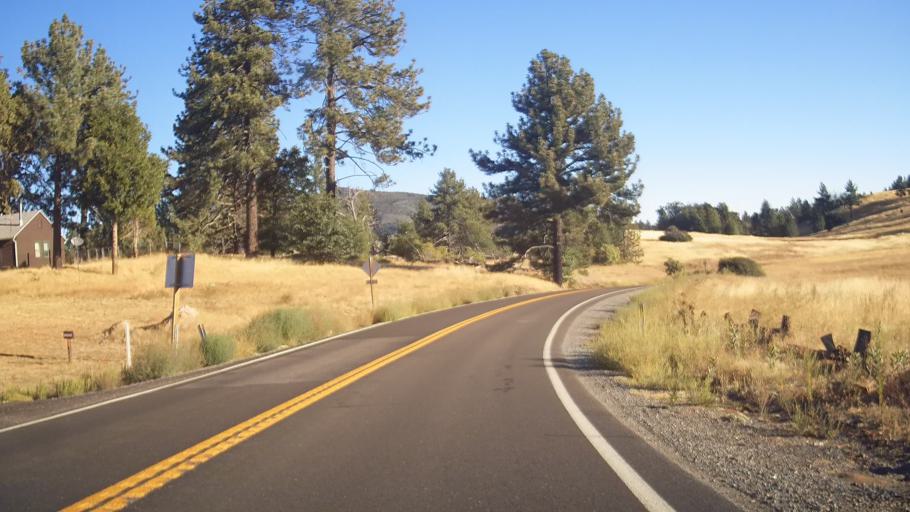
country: US
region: California
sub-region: San Diego County
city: Julian
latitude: 32.9718
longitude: -116.5771
